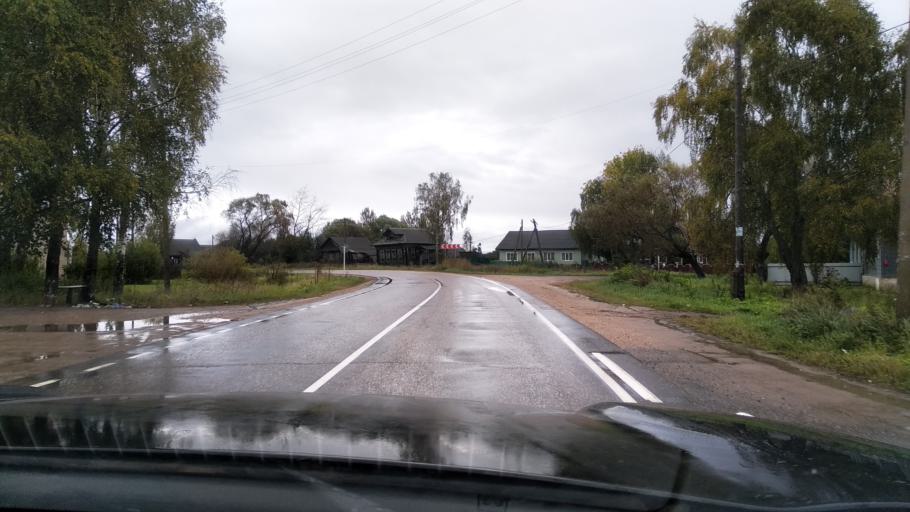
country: RU
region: Tverskaya
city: Kashin
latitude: 57.3281
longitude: 37.5223
